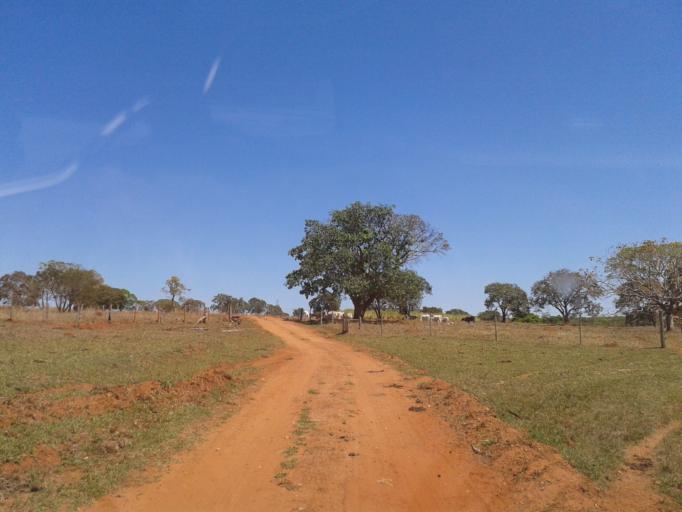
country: BR
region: Minas Gerais
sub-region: Ituiutaba
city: Ituiutaba
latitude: -19.1131
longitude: -49.2770
